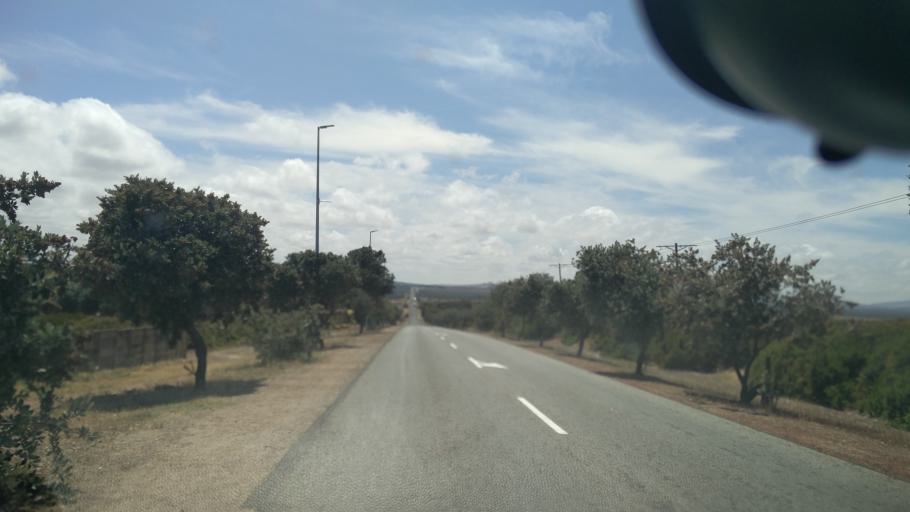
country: ZA
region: Western Cape
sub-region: City of Cape Town
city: Atlantis
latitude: -33.3442
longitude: 18.1638
